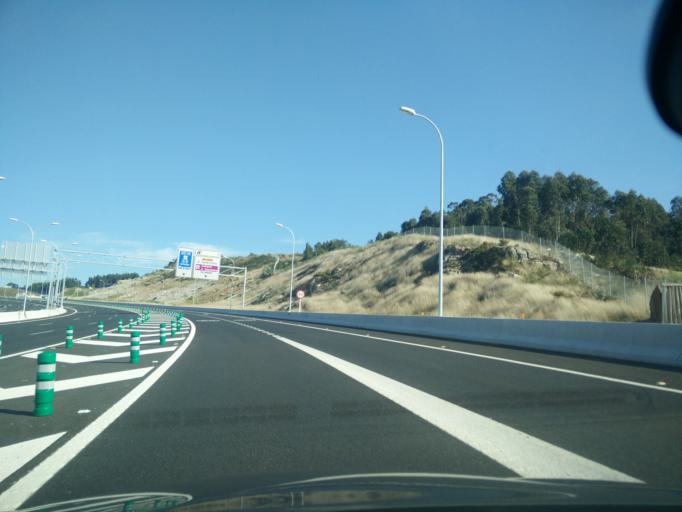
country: ES
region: Galicia
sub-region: Provincia da Coruna
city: Culleredo
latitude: 43.3250
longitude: -8.4204
